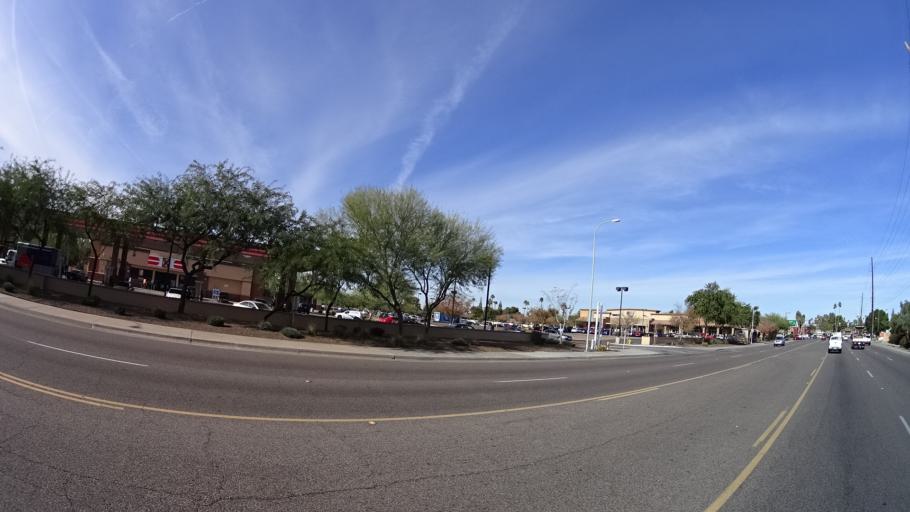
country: US
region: Arizona
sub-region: Maricopa County
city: Guadalupe
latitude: 33.3765
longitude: -111.9287
